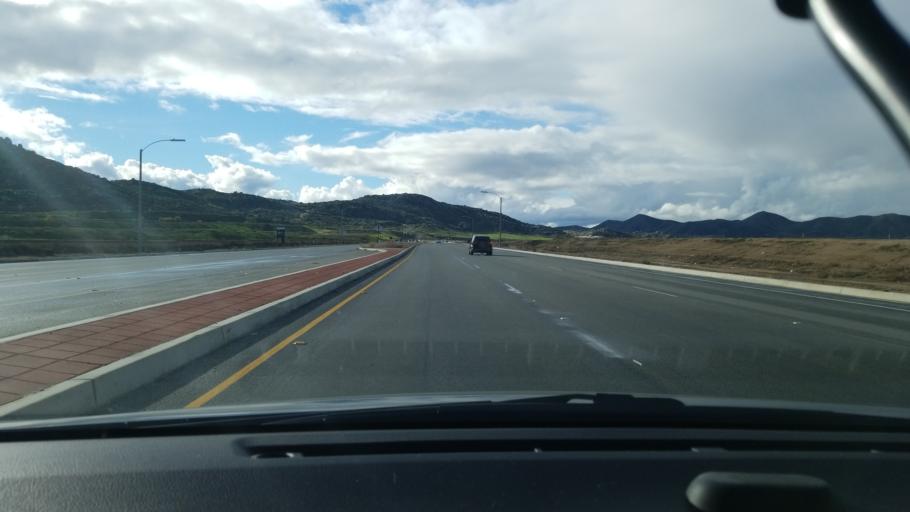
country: US
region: California
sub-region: Riverside County
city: Winchester
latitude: 33.6926
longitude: -117.1203
